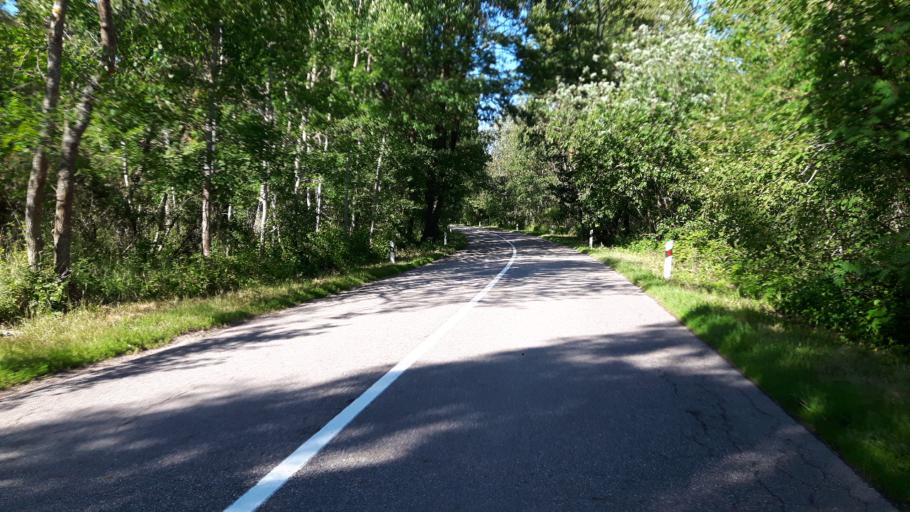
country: RU
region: Kaliningrad
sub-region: Zelenogradskiy Rayon
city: Zelenogradsk
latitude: 55.0951
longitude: 20.7406
